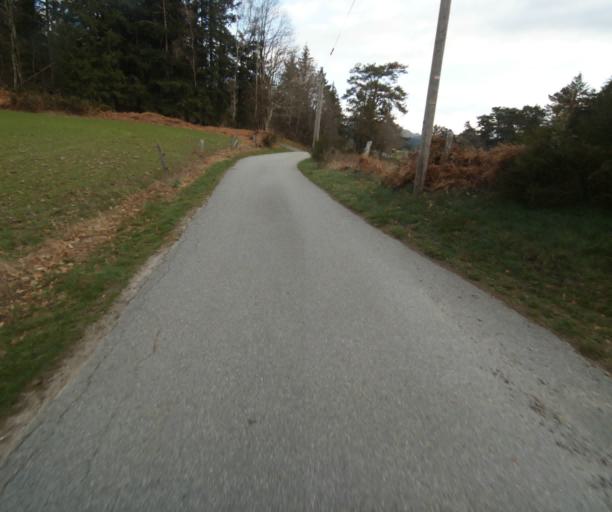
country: FR
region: Limousin
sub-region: Departement de la Correze
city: Correze
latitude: 45.3878
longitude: 1.8802
